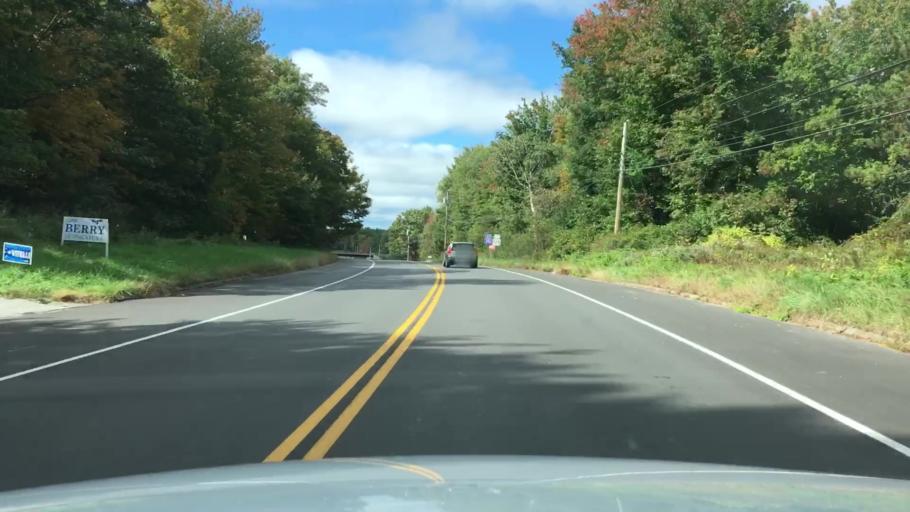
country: US
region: Maine
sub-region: Sagadahoc County
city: Topsham
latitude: 44.0162
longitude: -69.9141
